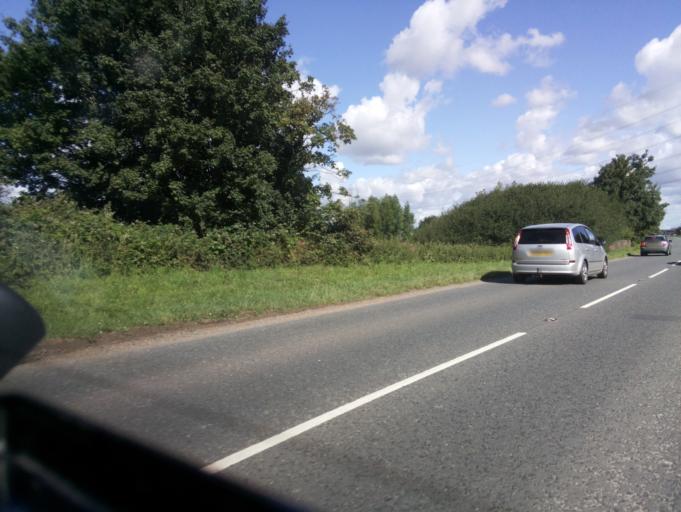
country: GB
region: England
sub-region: Gloucestershire
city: Newent
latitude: 51.8985
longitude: -2.3316
